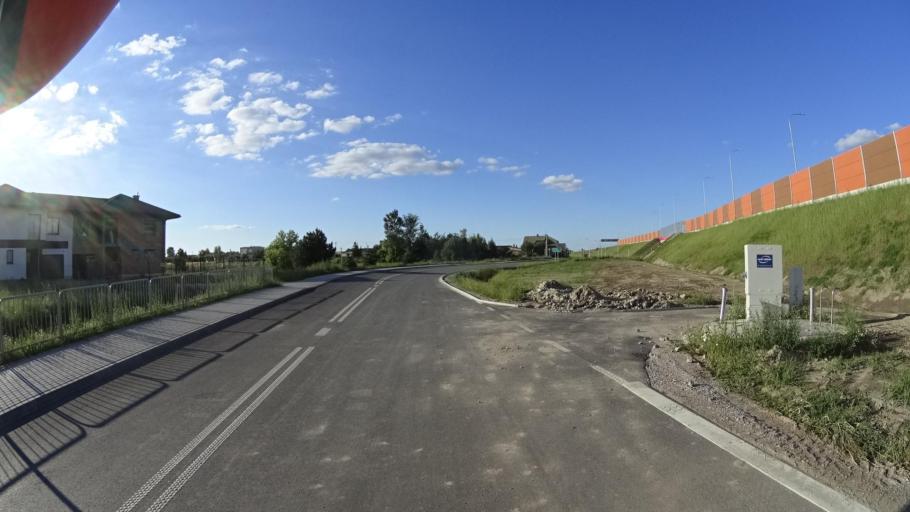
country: PL
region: Masovian Voivodeship
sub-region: Powiat piaseczynski
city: Lesznowola
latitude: 52.0919
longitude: 20.9696
